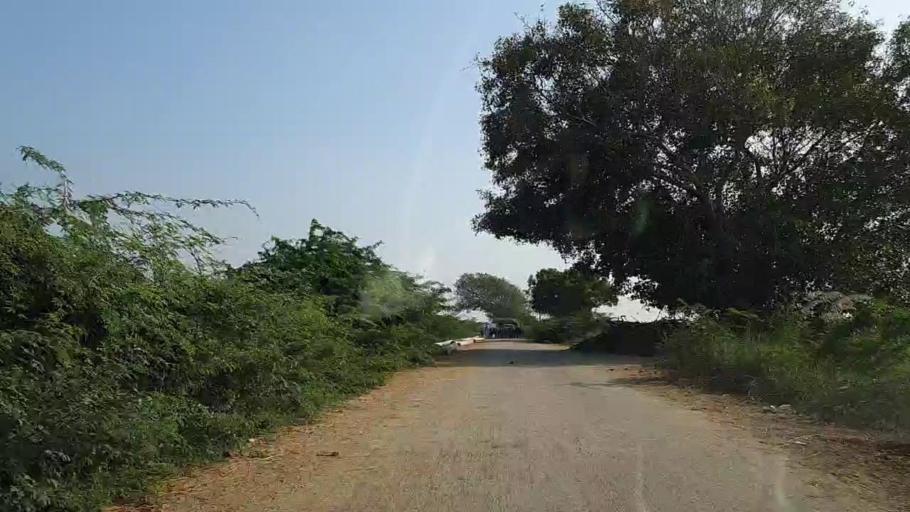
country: PK
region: Sindh
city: Mirpur Sakro
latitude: 24.6274
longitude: 67.6533
